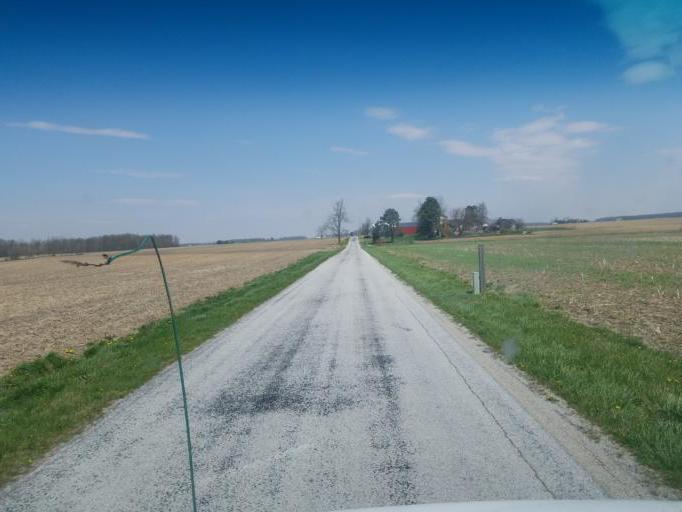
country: US
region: Ohio
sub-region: Hardin County
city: Kenton
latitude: 40.6856
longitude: -83.5471
